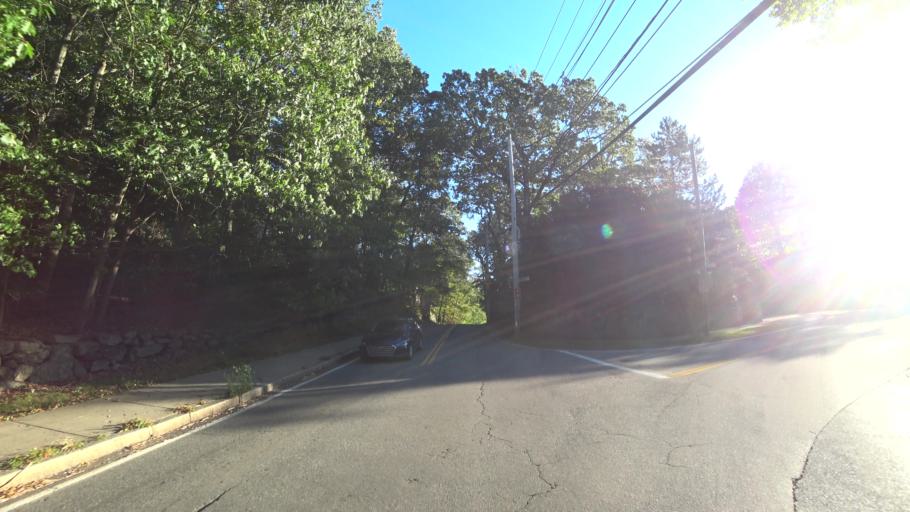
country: US
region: Massachusetts
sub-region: Norfolk County
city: Brookline
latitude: 42.3270
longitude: -71.1316
